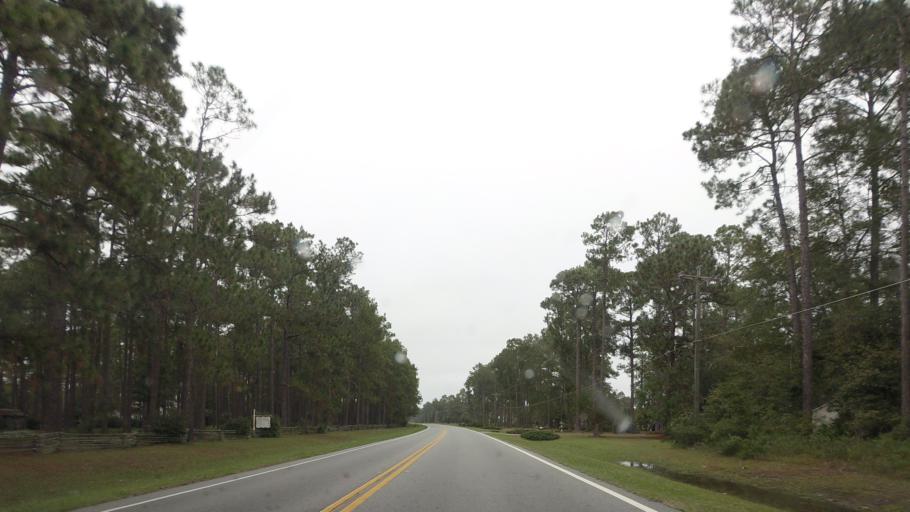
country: US
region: Georgia
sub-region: Berrien County
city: Nashville
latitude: 31.2539
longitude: -83.2403
